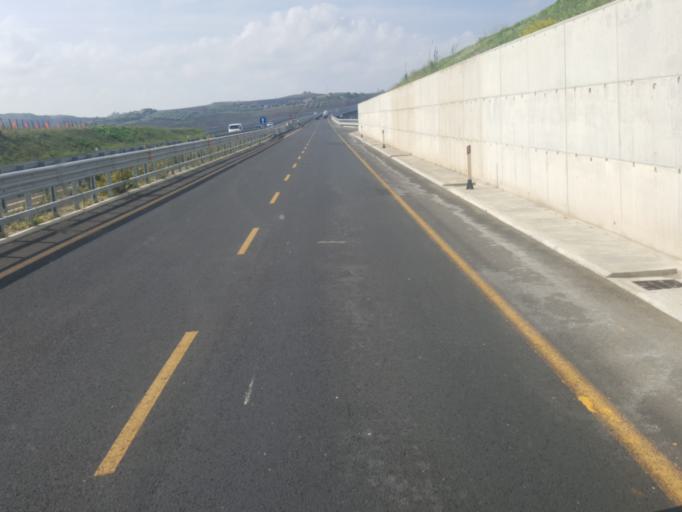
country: IT
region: Sicily
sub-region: Provincia di Caltanissetta
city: Serradifalco
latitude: 37.4340
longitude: 13.9376
